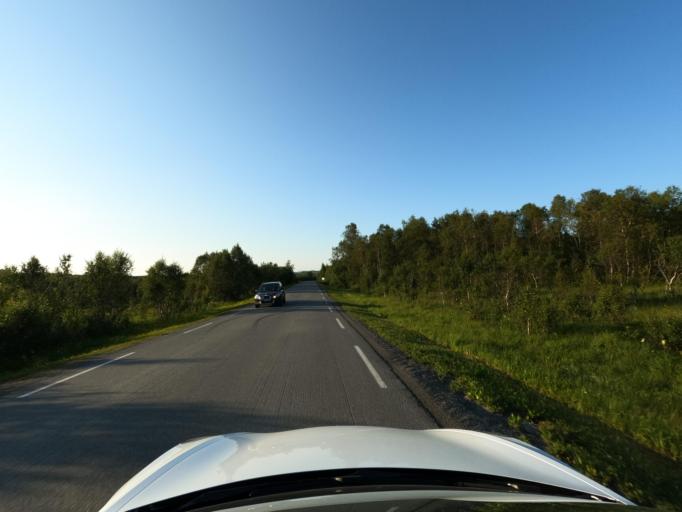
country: NO
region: Troms
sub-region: Skanland
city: Evenskjer
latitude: 68.4820
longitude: 16.7113
